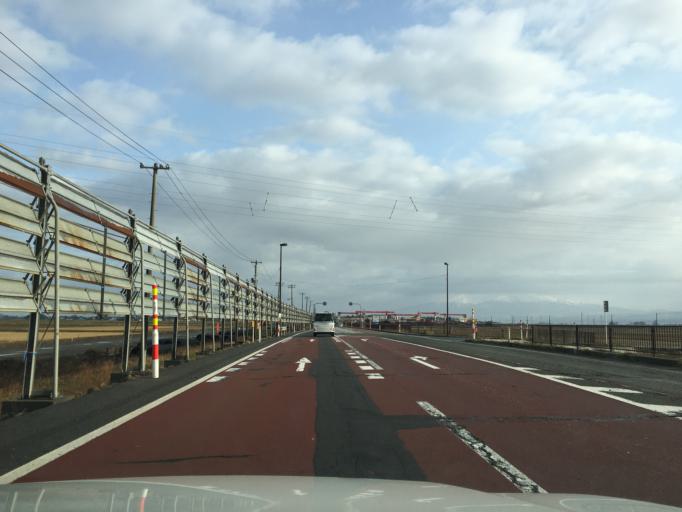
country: JP
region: Yamagata
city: Sakata
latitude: 38.8346
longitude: 139.8477
